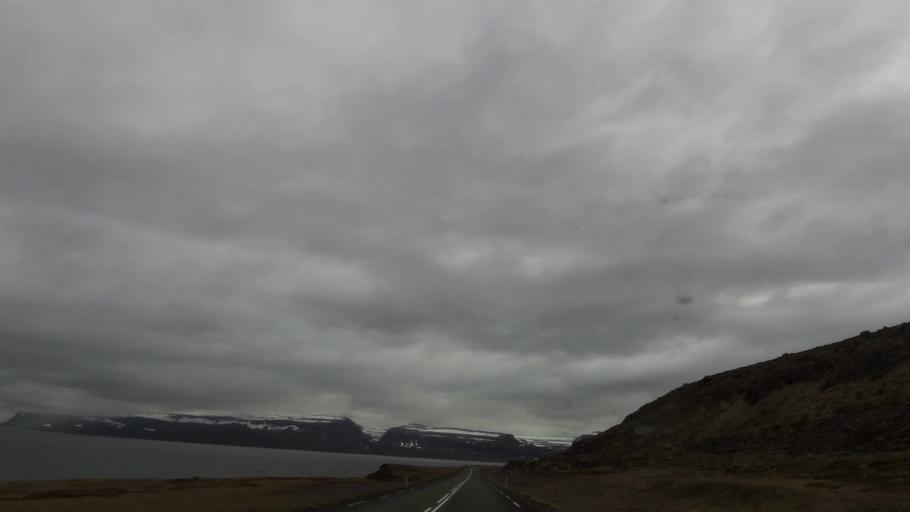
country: IS
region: Westfjords
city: Isafjoerdur
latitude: 66.0512
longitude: -22.7657
